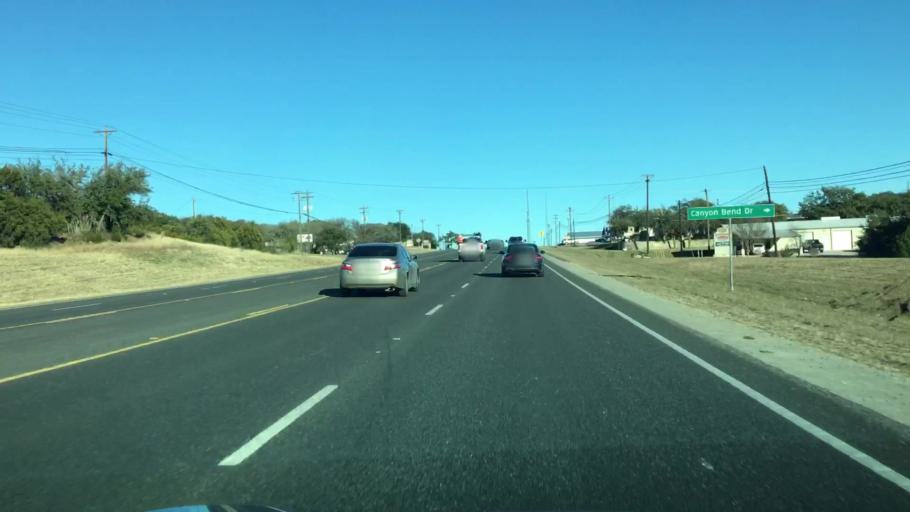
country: US
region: Texas
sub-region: Hays County
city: Dripping Springs
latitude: 30.1961
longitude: -98.0262
